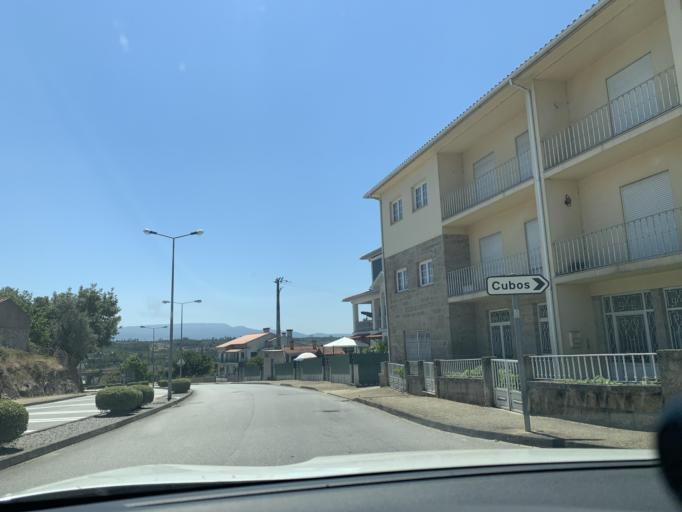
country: PT
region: Viseu
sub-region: Mangualde
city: Mangualde
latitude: 40.5875
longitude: -7.7644
